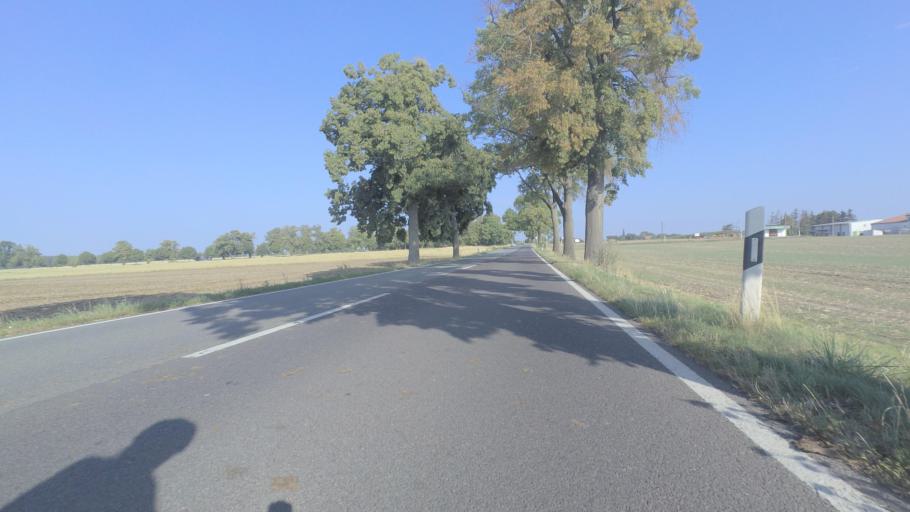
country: DE
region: Brandenburg
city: Fehrbellin
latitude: 52.7742
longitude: 12.8398
